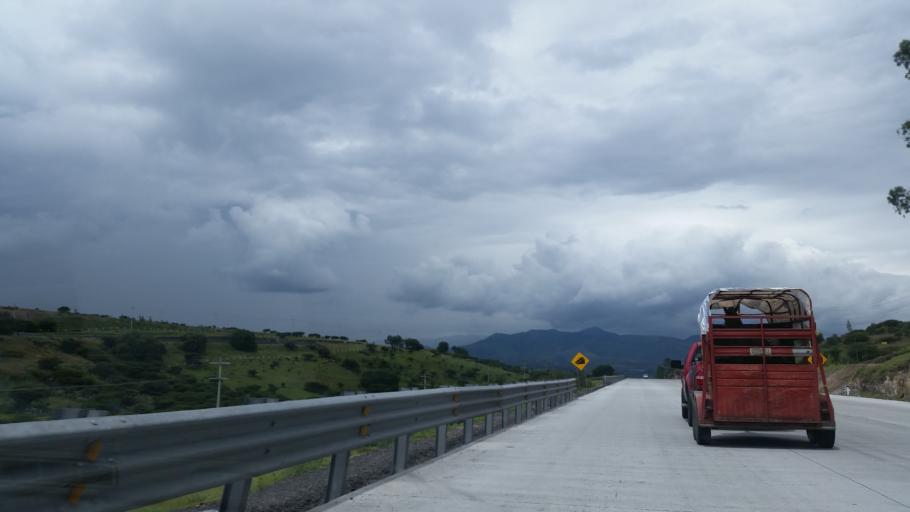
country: MX
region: Hidalgo
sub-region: Tepeji del Rio de Ocampo
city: Cantera de Villagran
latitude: 19.8570
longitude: -99.2943
